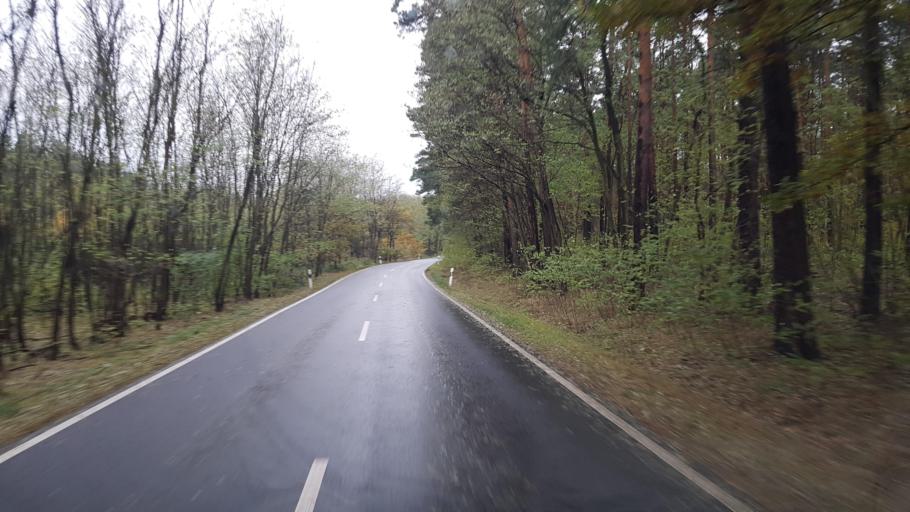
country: DE
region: Brandenburg
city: Drebkau
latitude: 51.6644
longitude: 14.2725
